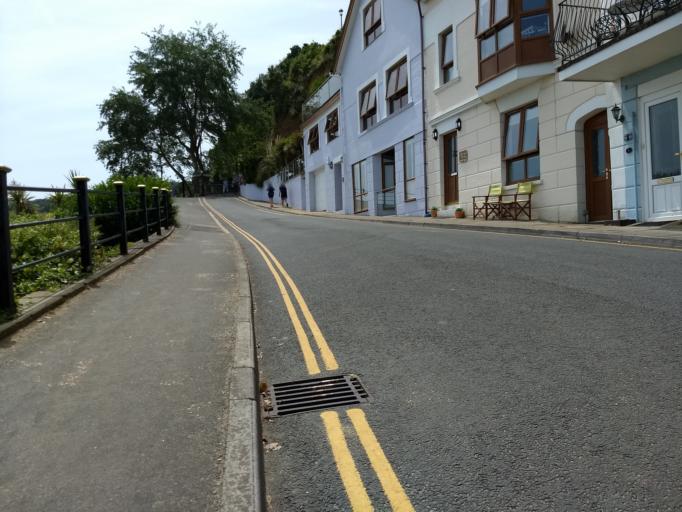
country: GB
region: England
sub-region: Isle of Wight
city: Shanklin
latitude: 50.6269
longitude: -1.1735
